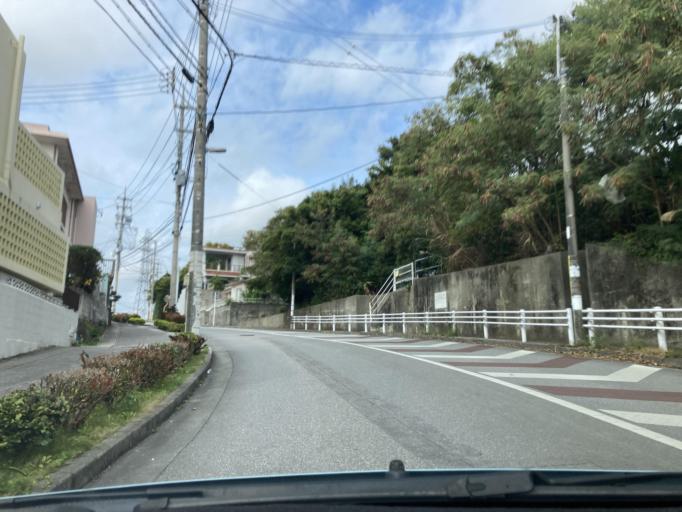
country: JP
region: Okinawa
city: Ginowan
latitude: 26.2036
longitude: 127.7508
